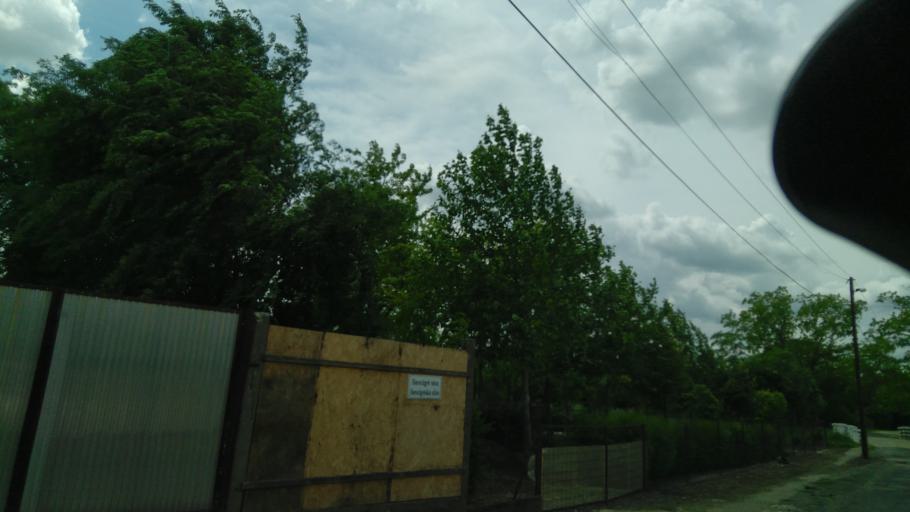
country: HU
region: Bekes
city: Totkomlos
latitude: 46.4146
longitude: 20.7288
